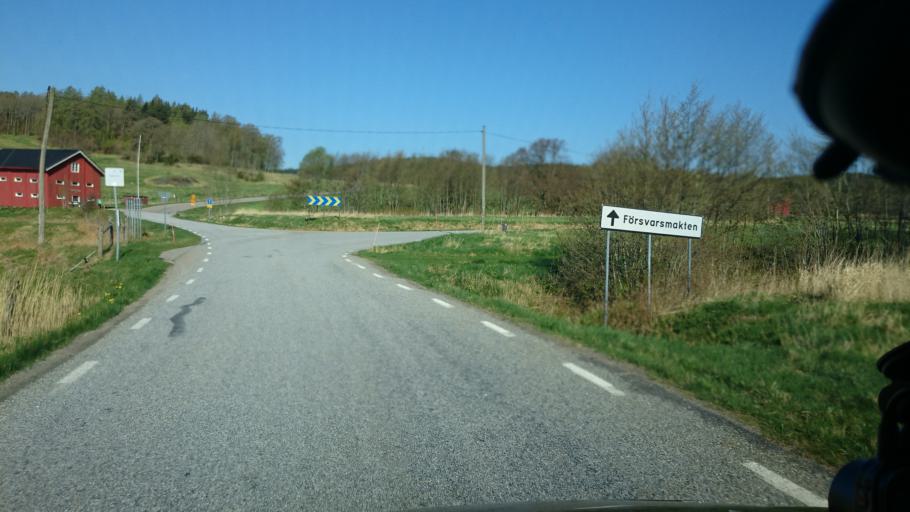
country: SE
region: Vaestra Goetaland
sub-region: Munkedals Kommun
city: Munkedal
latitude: 58.3921
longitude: 11.6542
